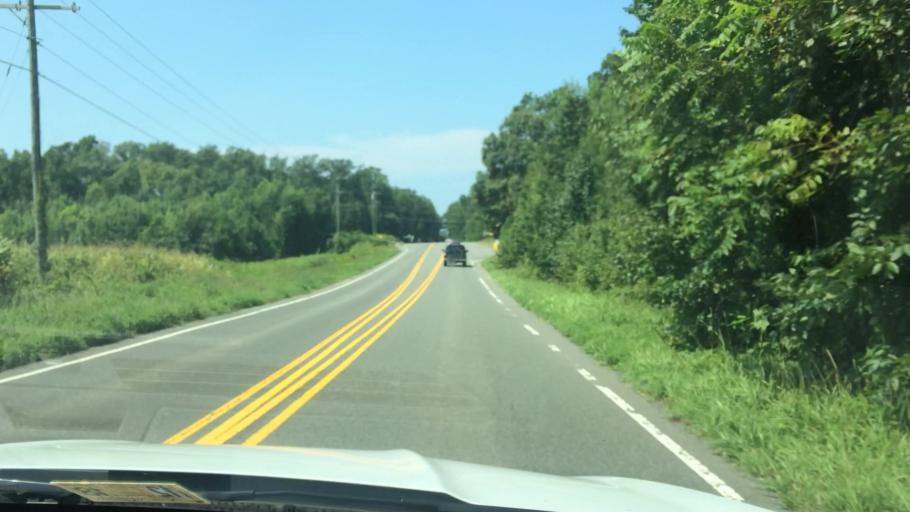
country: US
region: Virginia
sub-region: Henrico County
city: Sandston
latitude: 37.5271
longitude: -77.1663
